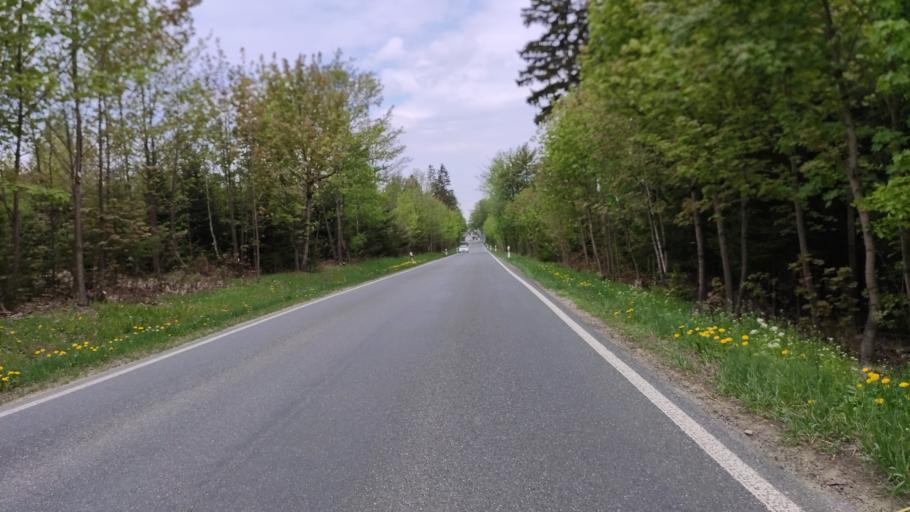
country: DE
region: Bavaria
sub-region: Upper Franconia
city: Reichenbach
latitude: 50.4687
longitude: 11.4629
